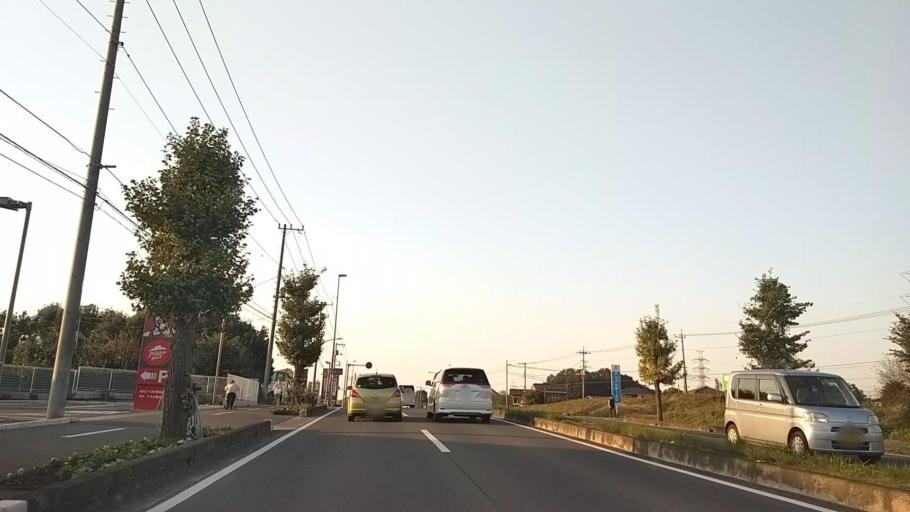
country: JP
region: Saitama
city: Sayama
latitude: 35.8610
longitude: 139.4295
